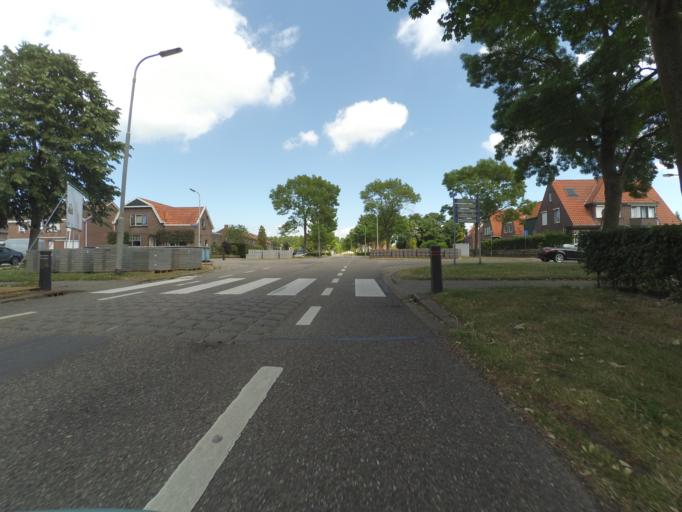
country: NL
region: Zeeland
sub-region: Gemeente Reimerswaal
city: Yerseke
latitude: 51.4489
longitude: 4.0037
